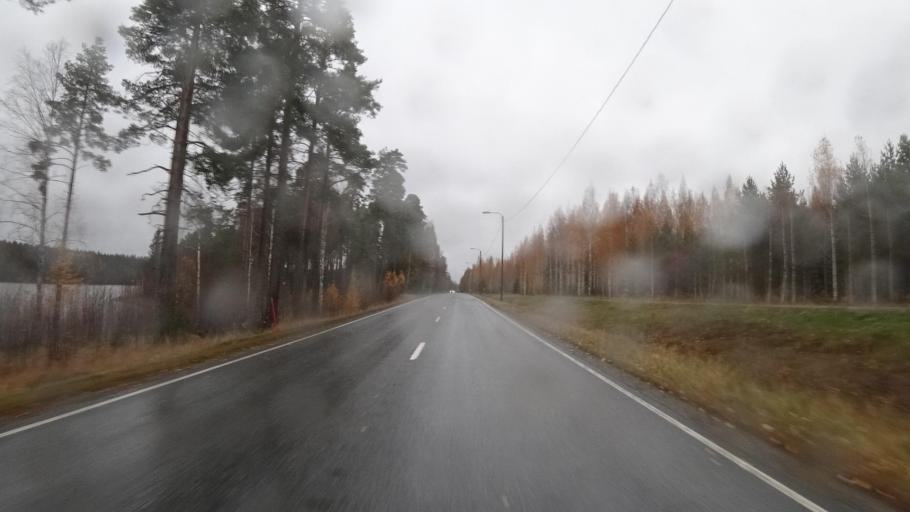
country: FI
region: Northern Savo
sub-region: Koillis-Savo
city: Tuusniemi
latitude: 62.8347
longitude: 28.4597
